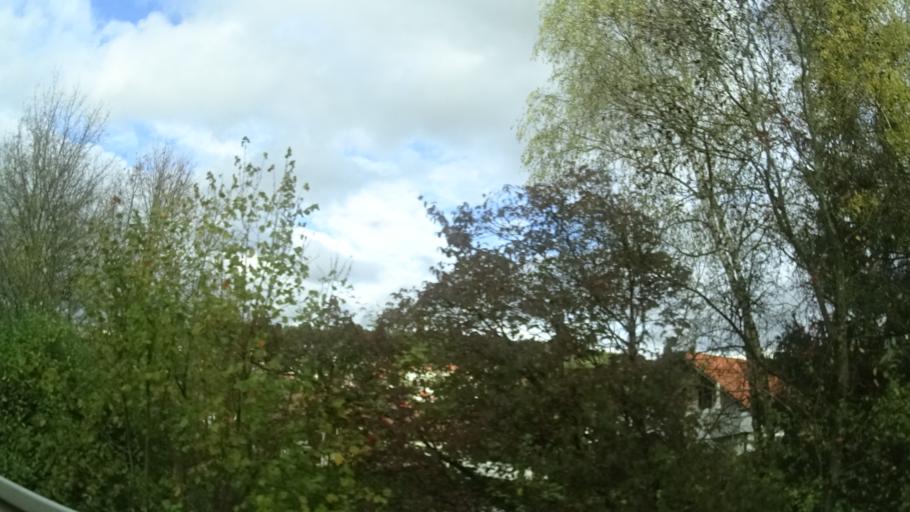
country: DE
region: Bavaria
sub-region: Regierungsbezirk Unterfranken
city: Heustreu
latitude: 50.3258
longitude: 10.2443
